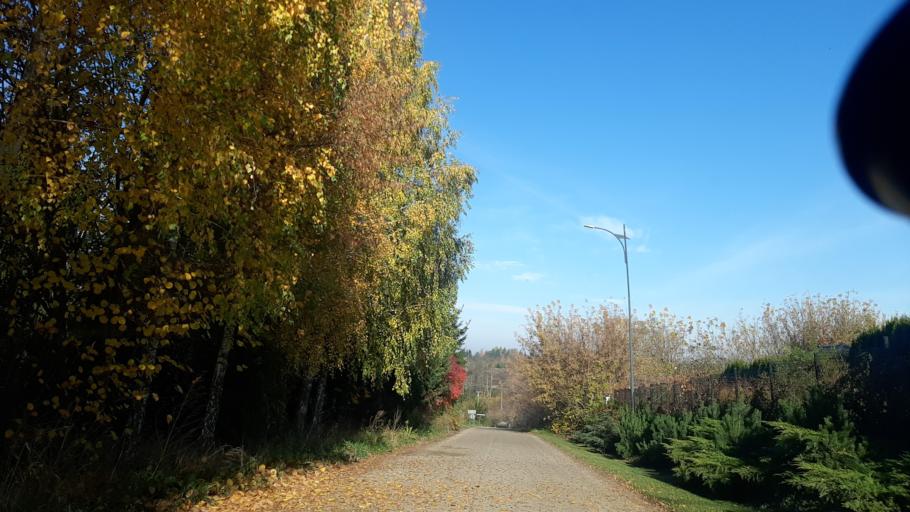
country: PL
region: Lublin Voivodeship
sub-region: Powiat lubelski
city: Lublin
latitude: 51.3101
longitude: 22.5204
